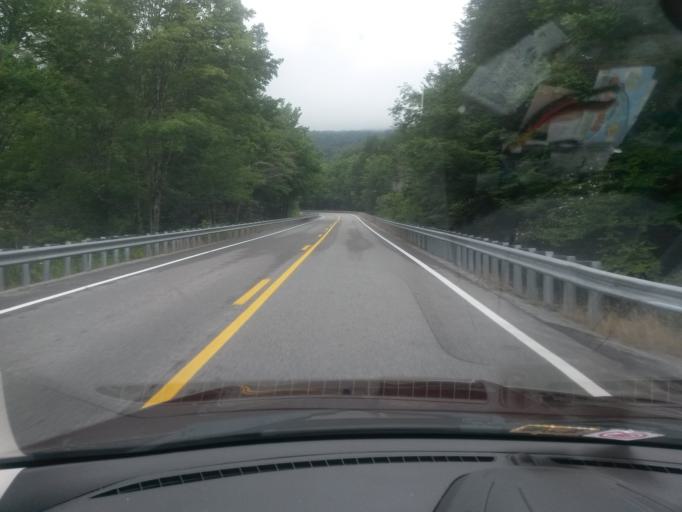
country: US
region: West Virginia
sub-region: Randolph County
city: Elkins
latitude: 38.6251
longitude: -79.8990
